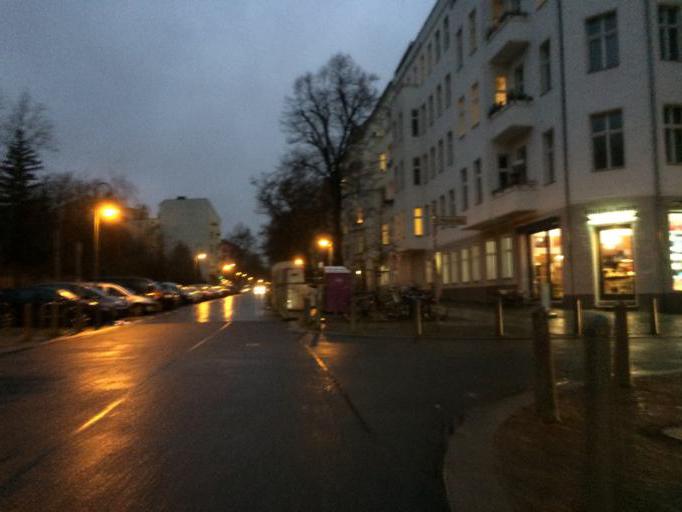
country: DE
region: Berlin
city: Prenzlauer Berg Bezirk
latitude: 52.5307
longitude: 13.4227
